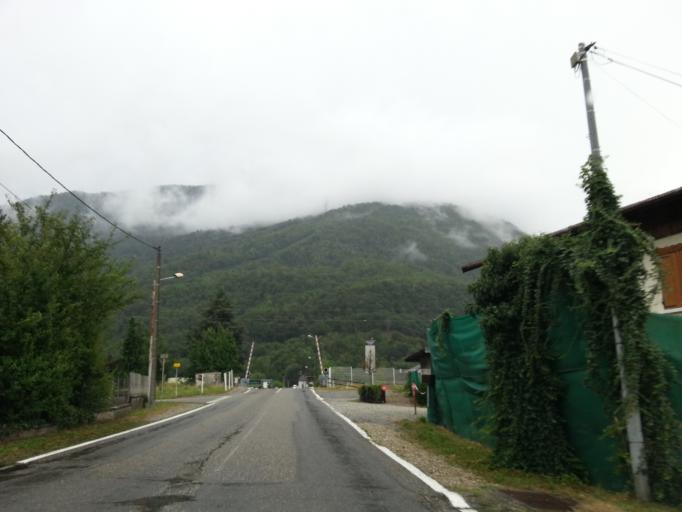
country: FR
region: Rhone-Alpes
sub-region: Departement de la Savoie
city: Albertville
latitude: 45.6669
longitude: 6.3949
